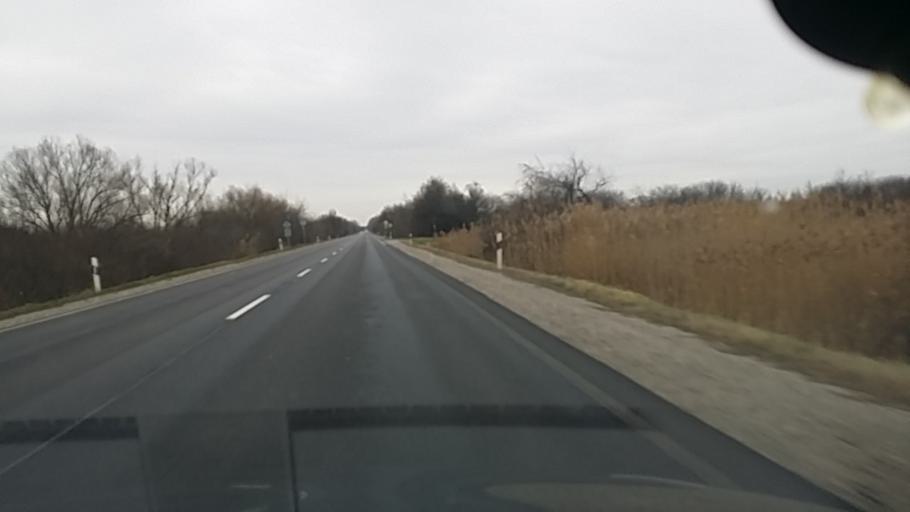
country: HU
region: Szabolcs-Szatmar-Bereg
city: Ujfeherto
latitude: 47.8523
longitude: 21.7039
